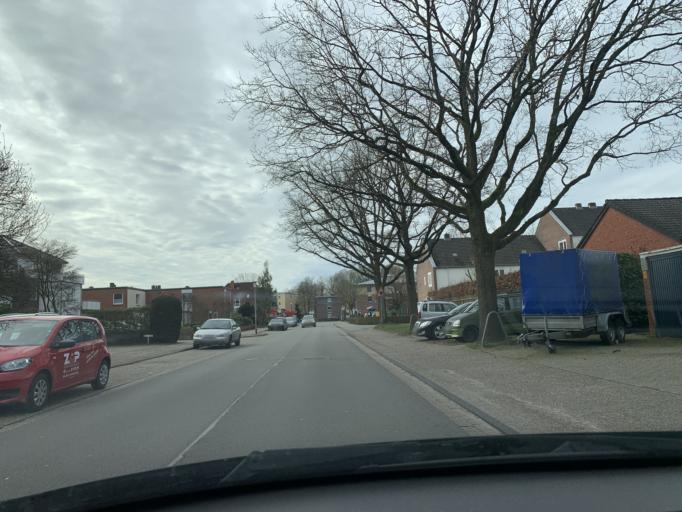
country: DE
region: Lower Saxony
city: Oldenburg
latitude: 53.1249
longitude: 8.1934
